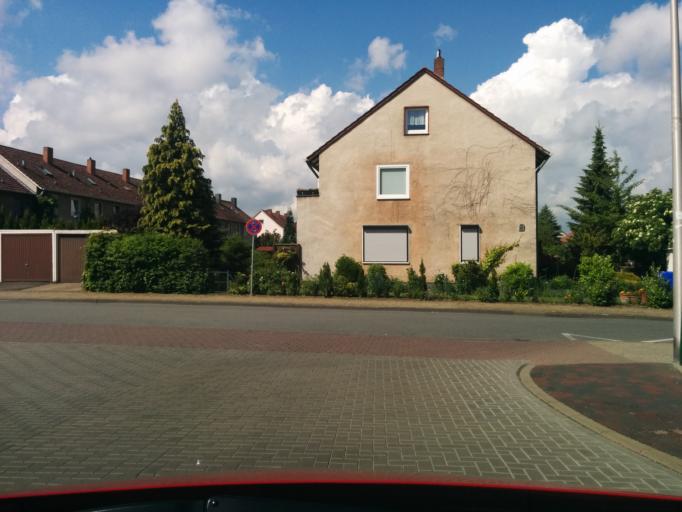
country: DE
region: Lower Saxony
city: Goslar
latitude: 51.9281
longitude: 10.4412
